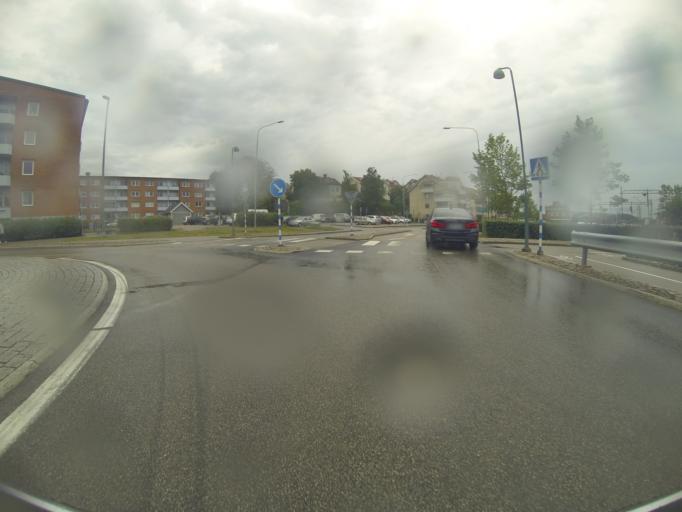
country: SE
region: Blekinge
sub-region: Ronneby Kommun
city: Ronneby
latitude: 56.2087
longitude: 15.2819
